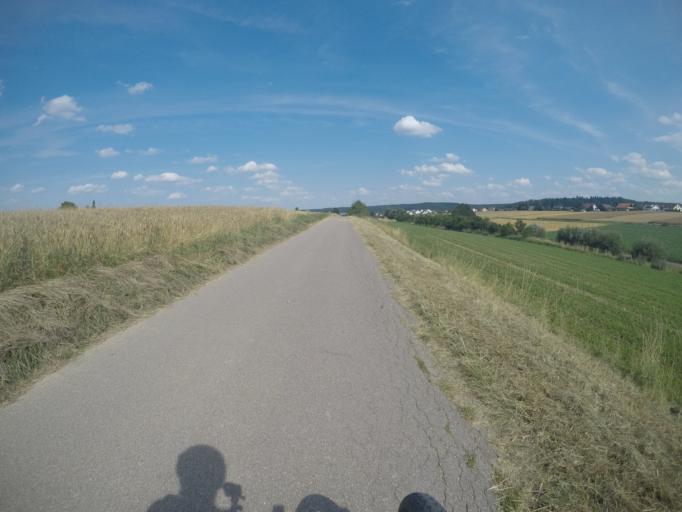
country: DE
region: Baden-Wuerttemberg
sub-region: Regierungsbezirk Stuttgart
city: Nufringen
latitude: 48.6273
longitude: 8.8785
